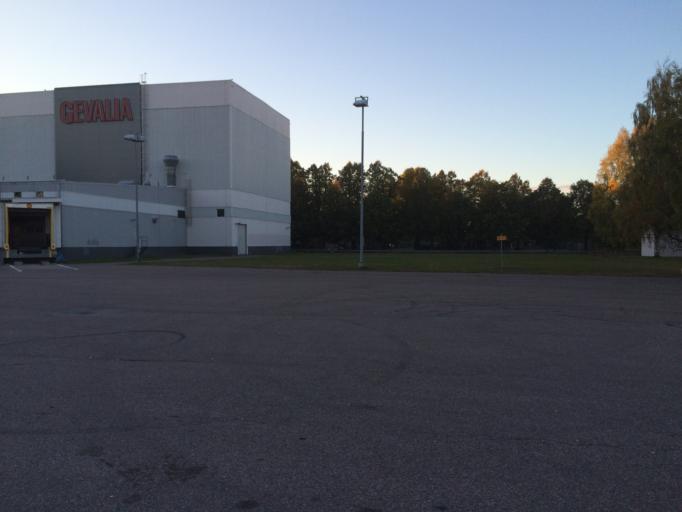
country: SE
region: Gaevleborg
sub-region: Gavle Kommun
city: Gavle
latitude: 60.6785
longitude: 17.1599
